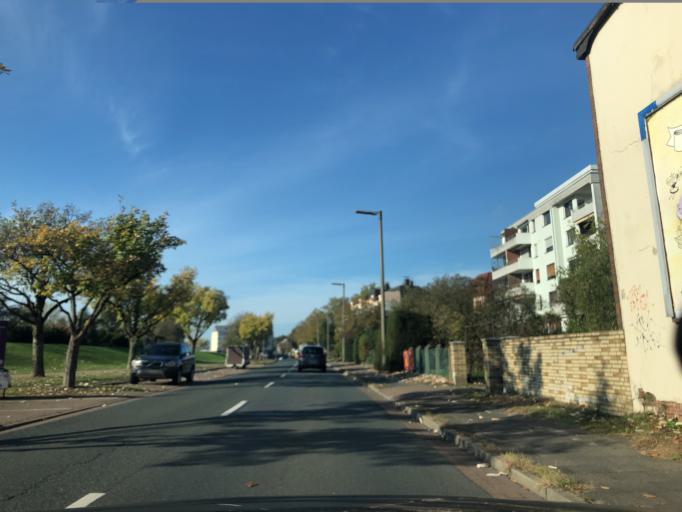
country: DE
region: Lower Saxony
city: Lemwerder
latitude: 53.1821
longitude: 8.5665
